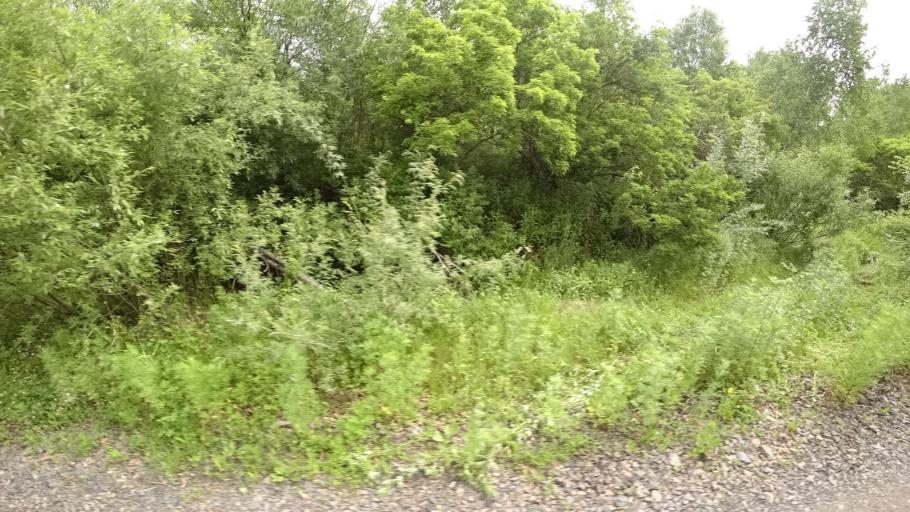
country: RU
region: Khabarovsk Krai
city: Amursk
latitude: 49.9002
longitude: 136.1499
